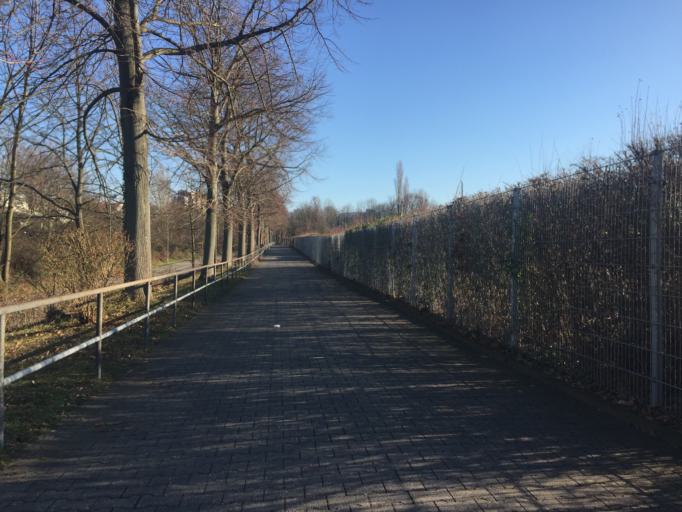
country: DE
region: Hesse
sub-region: Regierungsbezirk Darmstadt
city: Frankfurt am Main
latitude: 50.1470
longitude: 8.6791
